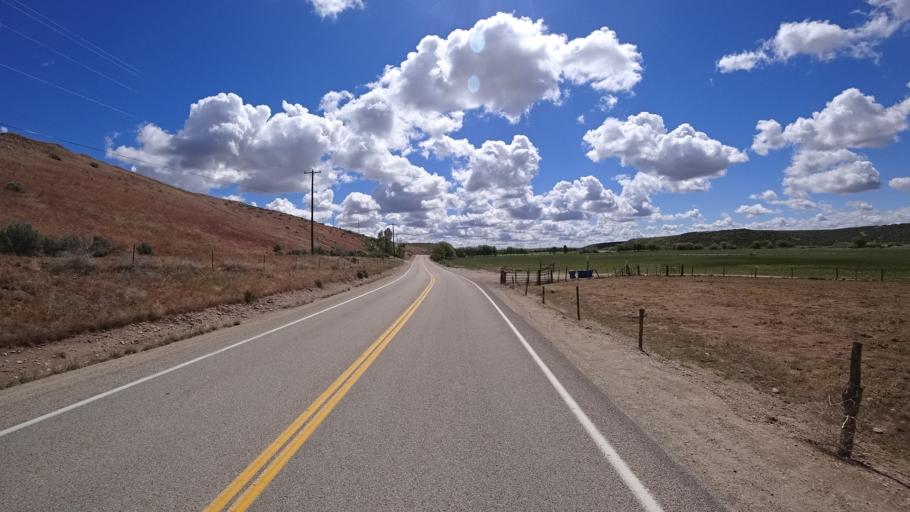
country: US
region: Idaho
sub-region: Ada County
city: Garden City
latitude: 43.4998
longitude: -116.2881
